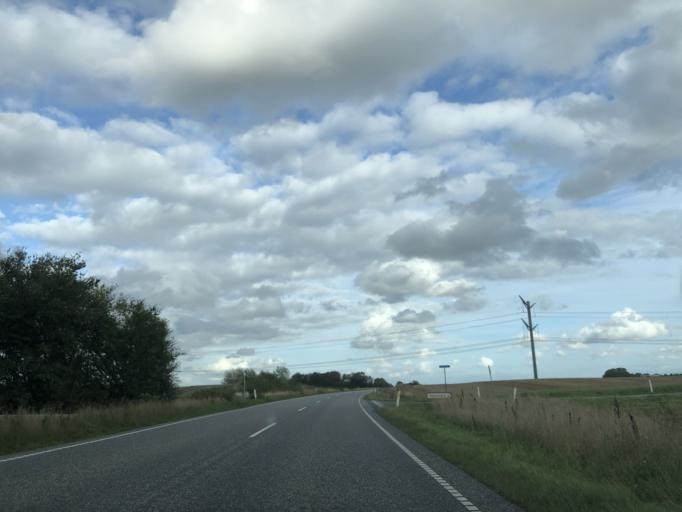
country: DK
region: Central Jutland
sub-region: Silkeborg Kommune
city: Kjellerup
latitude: 56.3120
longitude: 9.5200
